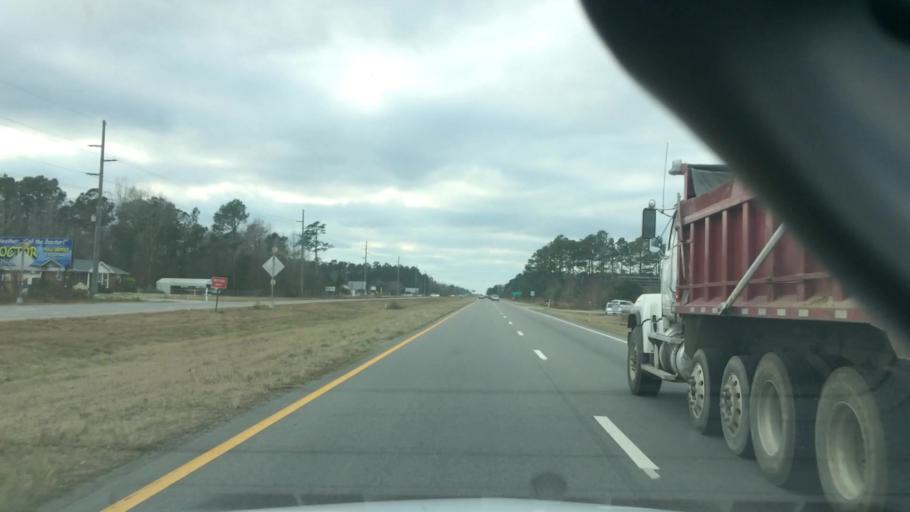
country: US
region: North Carolina
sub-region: Brunswick County
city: Sunset Beach
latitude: 33.9464
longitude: -78.5033
